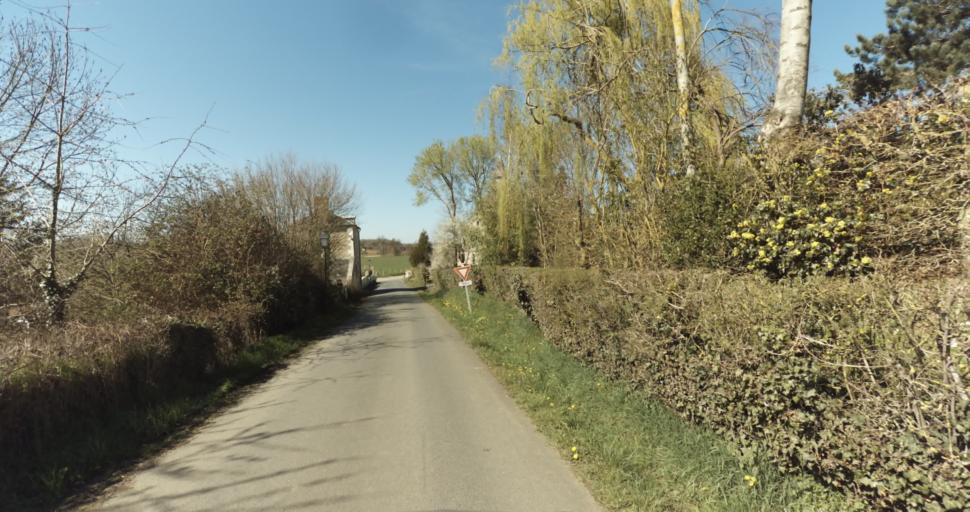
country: FR
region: Lower Normandy
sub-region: Departement du Calvados
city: Saint-Pierre-sur-Dives
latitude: 49.0519
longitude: -0.0221
